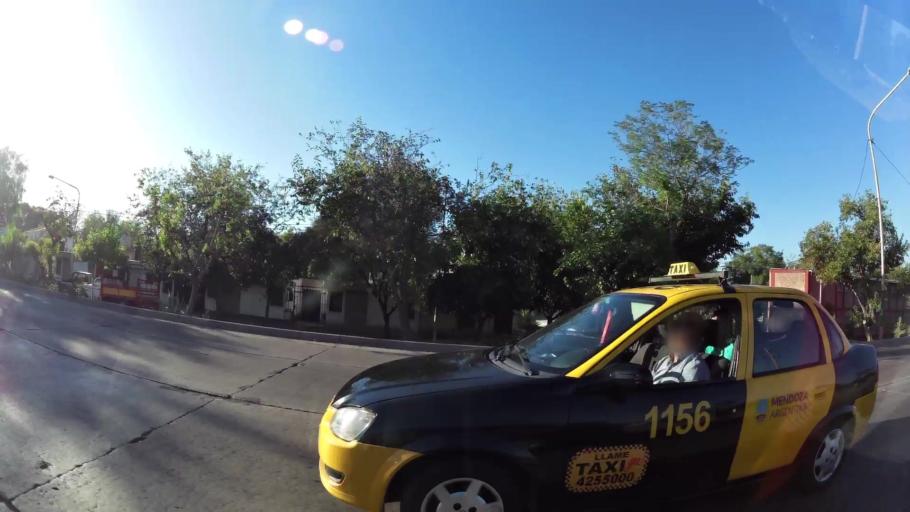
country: AR
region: Mendoza
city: Mendoza
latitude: -32.8733
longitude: -68.8186
